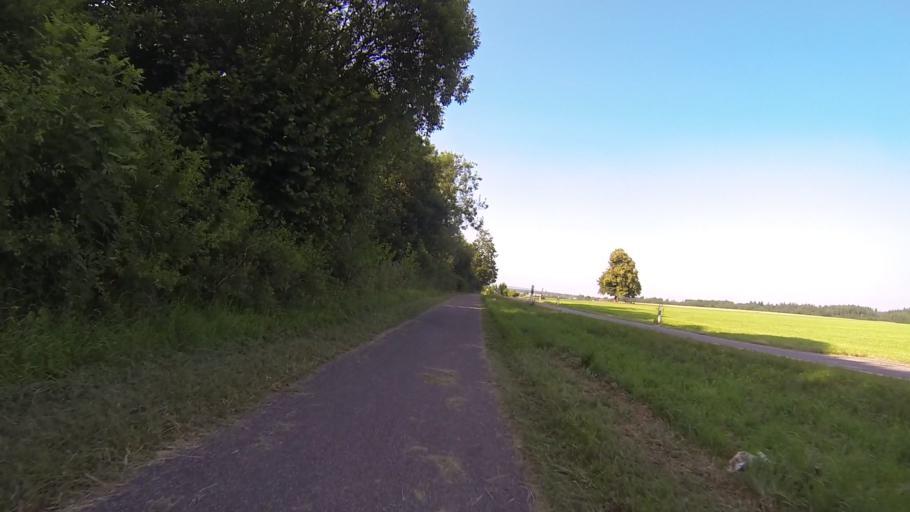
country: DE
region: Baden-Wuerttemberg
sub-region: Tuebingen Region
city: Staig
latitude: 48.3237
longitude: 9.9685
